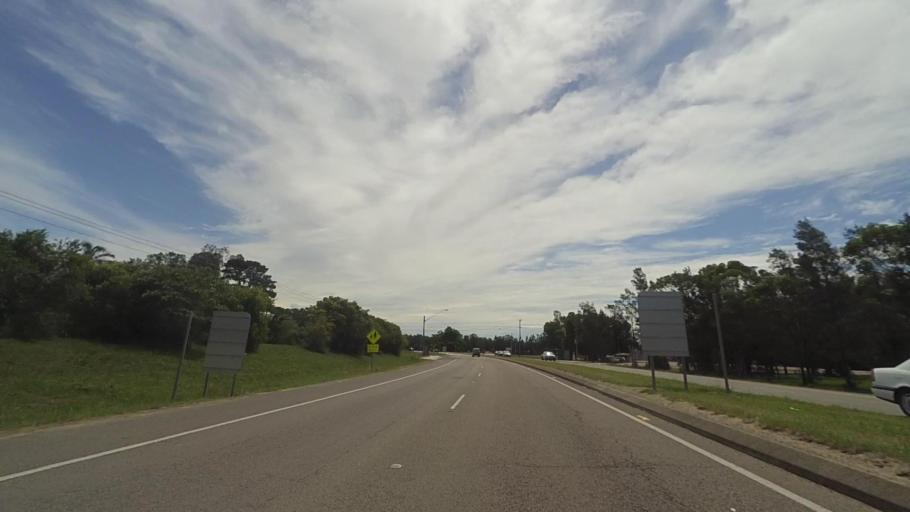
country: AU
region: New South Wales
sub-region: Port Stephens Shire
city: Medowie
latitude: -32.7888
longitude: 151.9053
